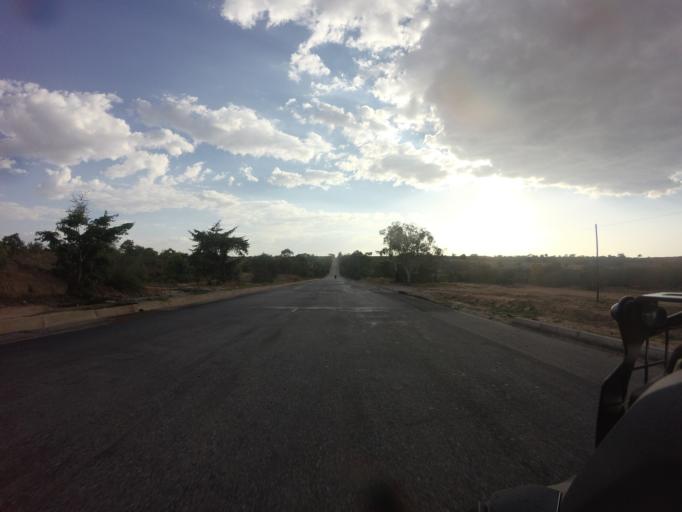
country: AO
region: Huila
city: Lubango
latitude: -14.7280
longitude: 13.8832
